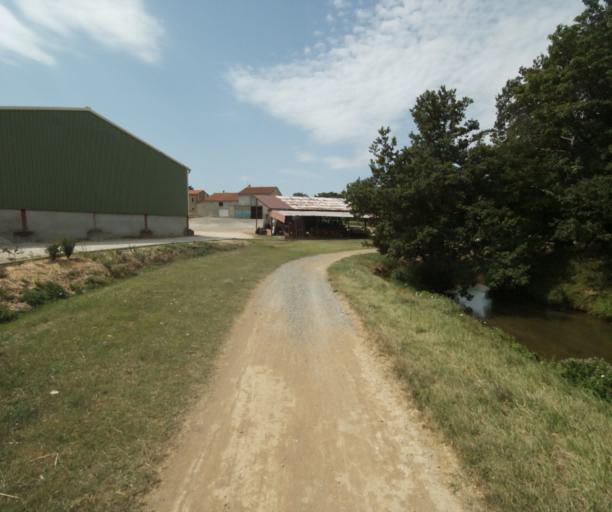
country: FR
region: Midi-Pyrenees
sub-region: Departement de la Haute-Garonne
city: Saint-Felix-Lauragais
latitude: 43.4282
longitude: 1.9102
